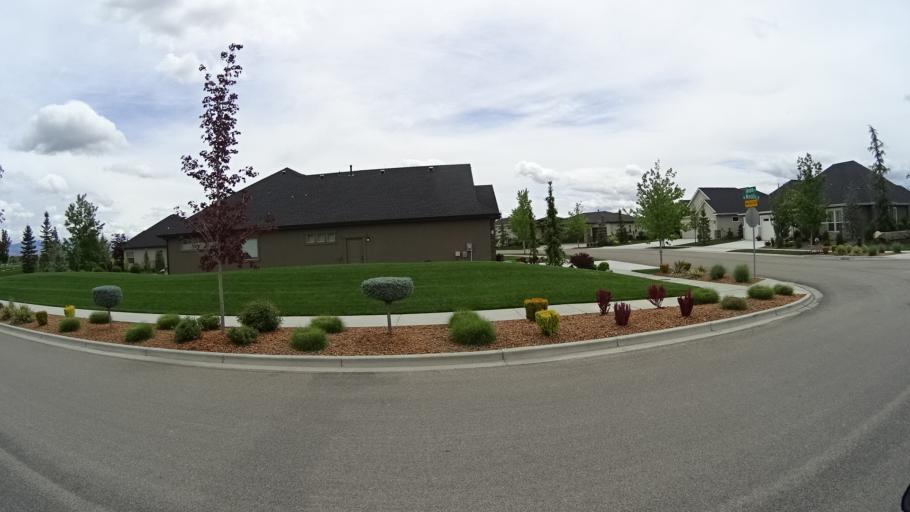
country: US
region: Idaho
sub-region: Ada County
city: Star
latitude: 43.7032
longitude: -116.4298
